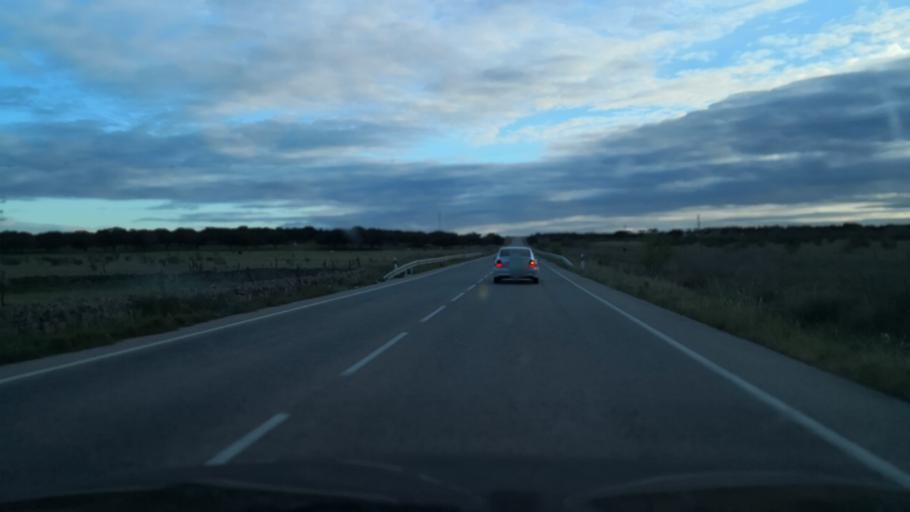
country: ES
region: Extremadura
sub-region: Provincia de Caceres
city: Malpartida de Caceres
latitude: 39.3722
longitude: -6.4544
